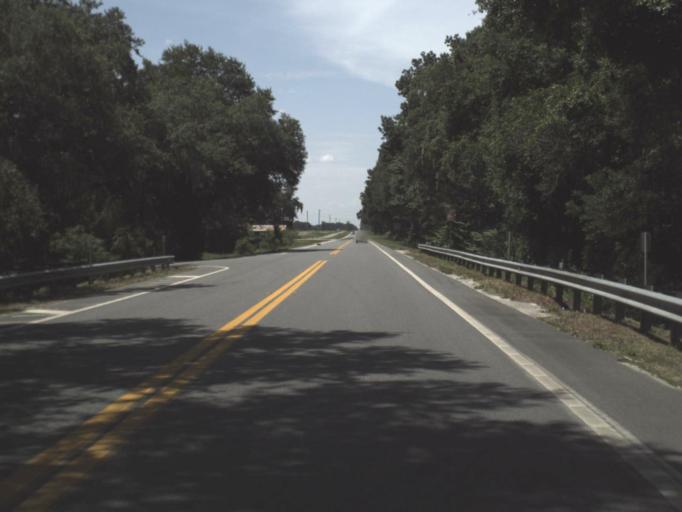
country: US
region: Florida
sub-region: Alachua County
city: High Springs
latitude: 29.9126
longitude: -82.8601
